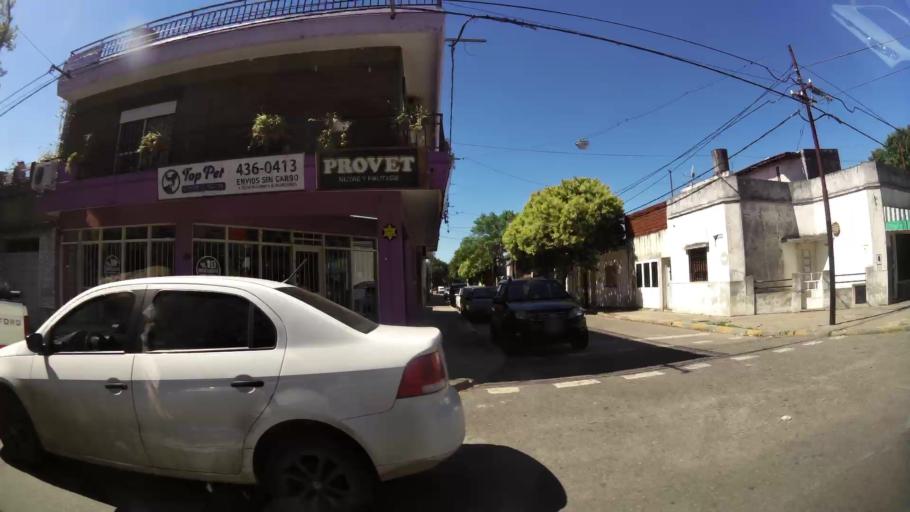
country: AR
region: Santa Fe
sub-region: Departamento de Rosario
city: Rosario
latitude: -32.9363
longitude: -60.6864
